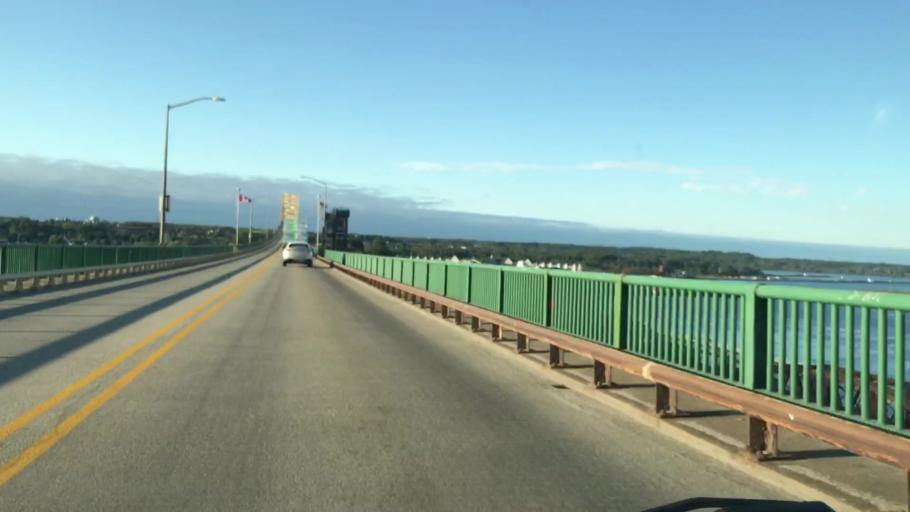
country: US
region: Michigan
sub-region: Chippewa County
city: Sault Ste. Marie
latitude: 46.5094
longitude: -84.3604
